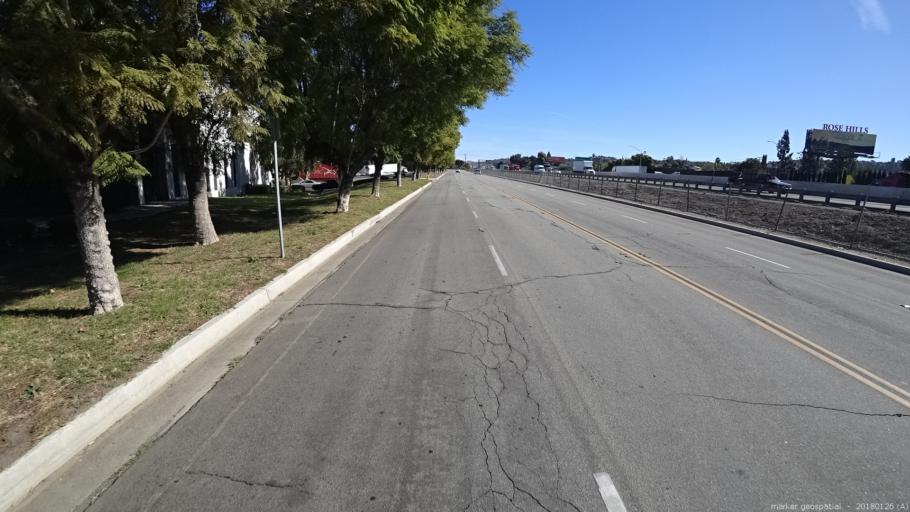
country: US
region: California
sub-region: Los Angeles County
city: Walnut
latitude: 33.9976
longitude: -117.8647
